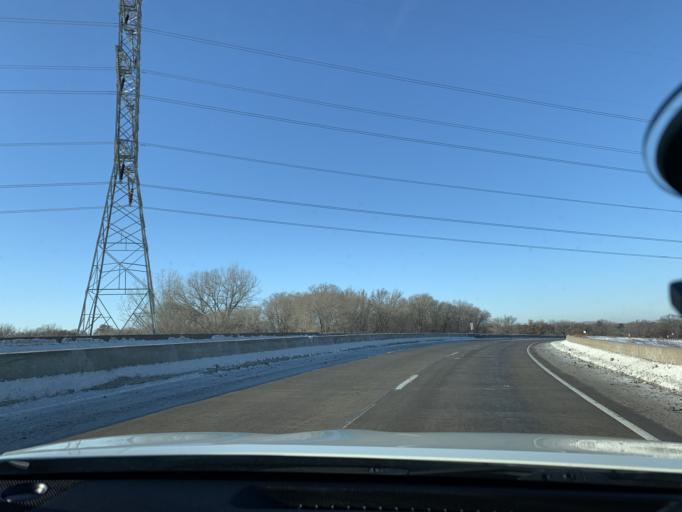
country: US
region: Minnesota
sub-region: Anoka County
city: Coon Rapids
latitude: 45.1463
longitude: -93.2907
